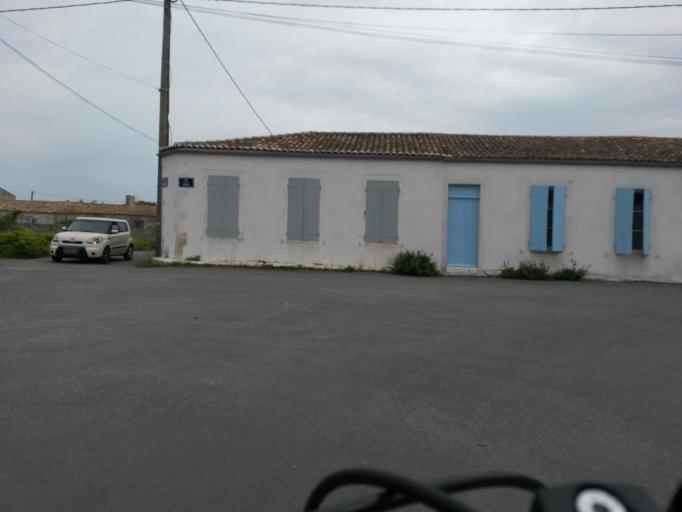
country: FR
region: Poitou-Charentes
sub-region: Departement de la Charente-Maritime
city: Dolus-d'Oleron
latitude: 45.9373
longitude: -1.3556
